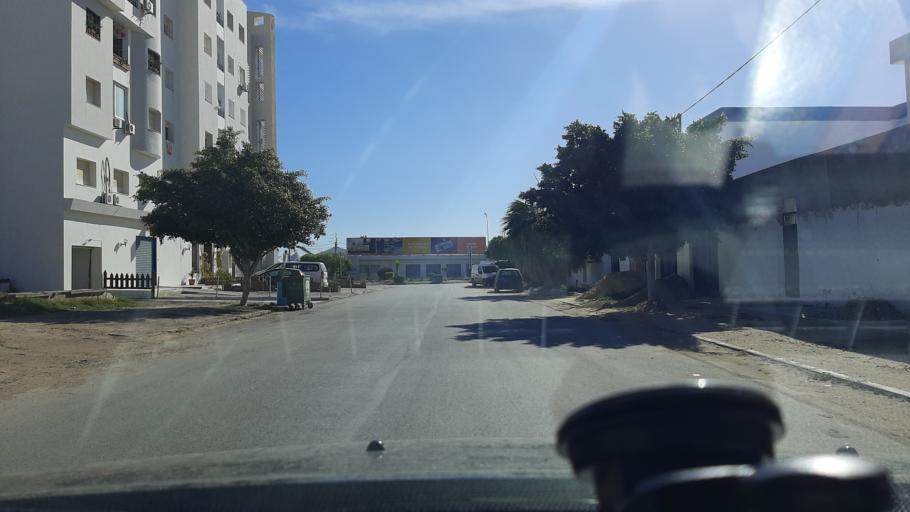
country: TN
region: Safaqis
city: Sfax
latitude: 34.7280
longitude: 10.7417
